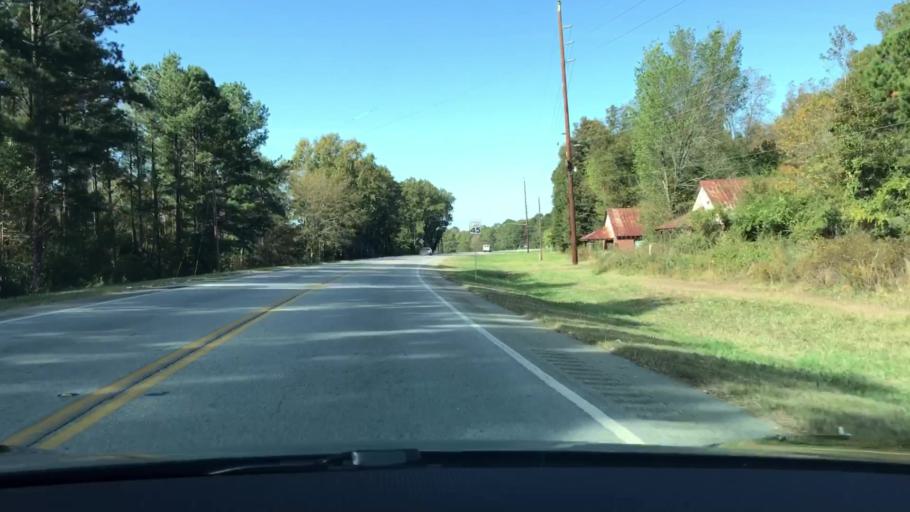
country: US
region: Georgia
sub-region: Warren County
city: Warrenton
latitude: 33.4000
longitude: -82.6639
